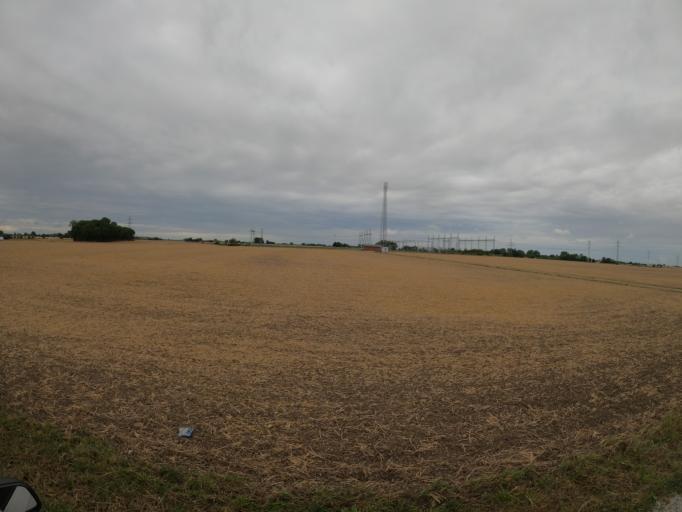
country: SE
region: Skane
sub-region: Lunds Kommun
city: Lund
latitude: 55.7406
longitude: 13.1496
